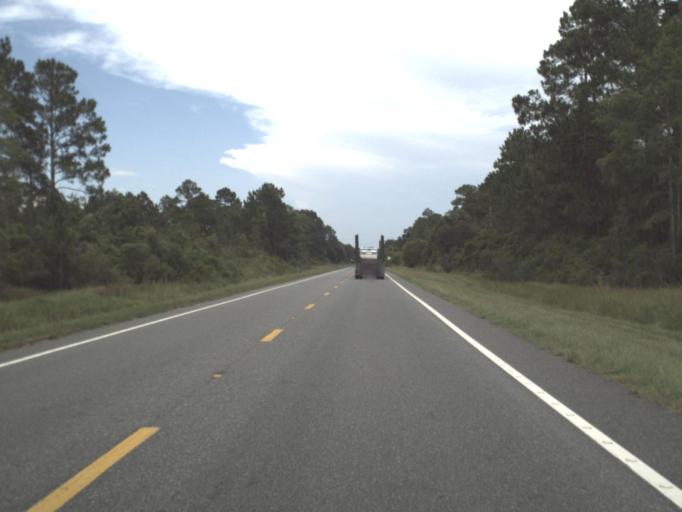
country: US
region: Florida
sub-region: Taylor County
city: Perry
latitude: 30.1278
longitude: -83.3746
